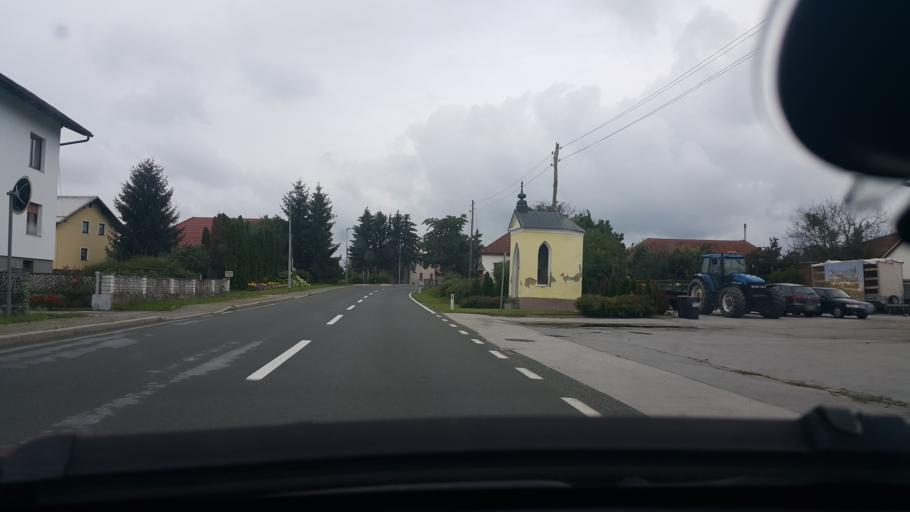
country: SI
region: Zavrc
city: Zavrc
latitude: 46.4138
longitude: 16.0928
